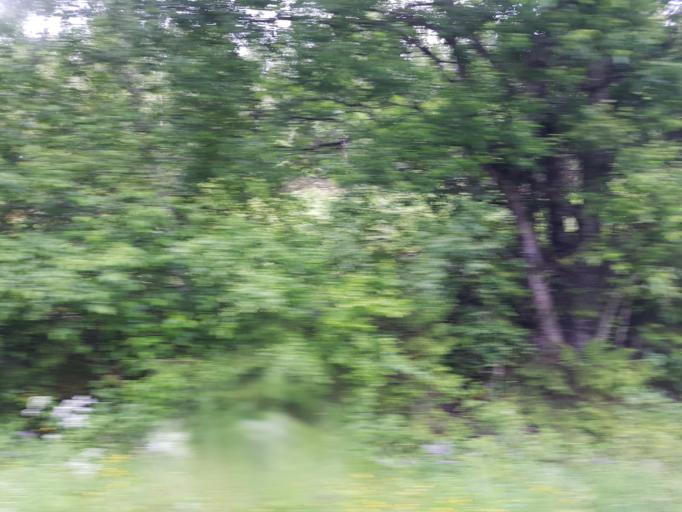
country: NO
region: Sor-Trondelag
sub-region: Selbu
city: Mebonden
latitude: 63.3662
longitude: 11.0741
